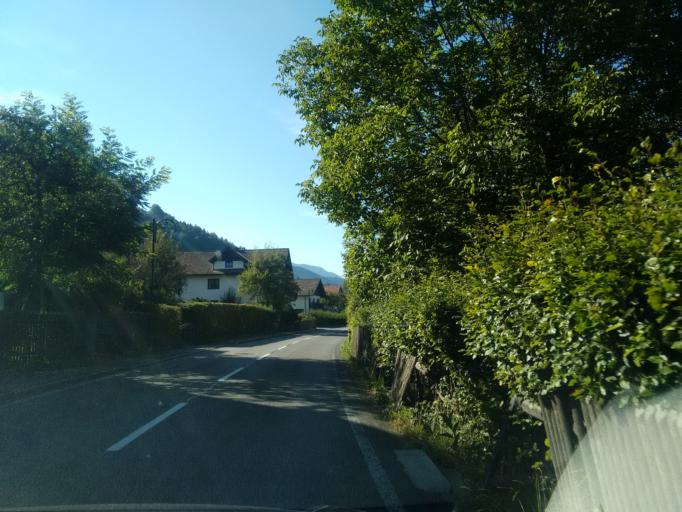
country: AT
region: Upper Austria
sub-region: Politischer Bezirk Vocklabruck
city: Attersee
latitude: 47.8957
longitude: 13.5714
